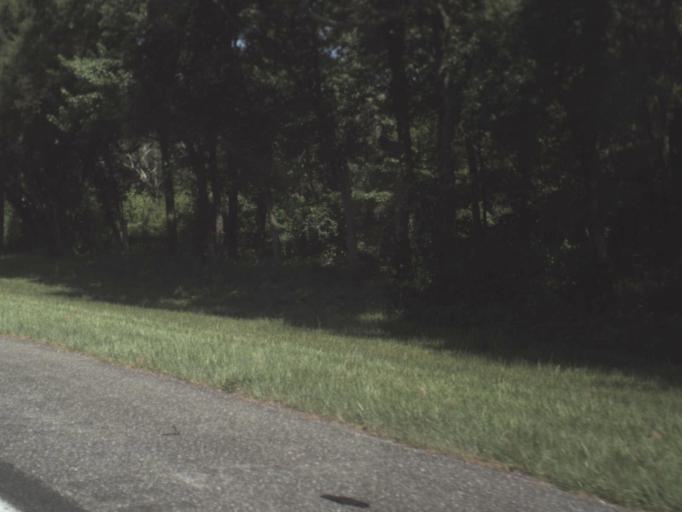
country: US
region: Florida
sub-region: Madison County
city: Madison
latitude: 30.4324
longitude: -83.6167
